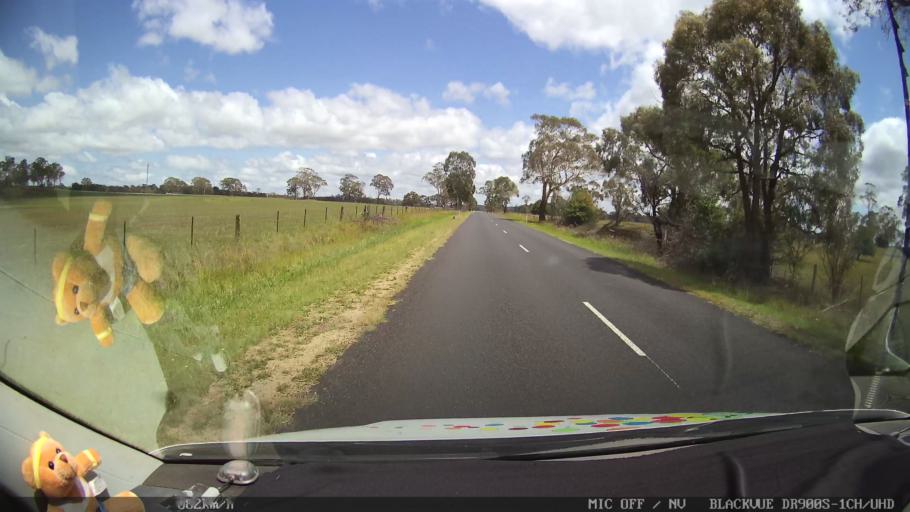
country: AU
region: New South Wales
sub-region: Glen Innes Severn
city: Glen Innes
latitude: -29.6234
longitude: 151.6704
